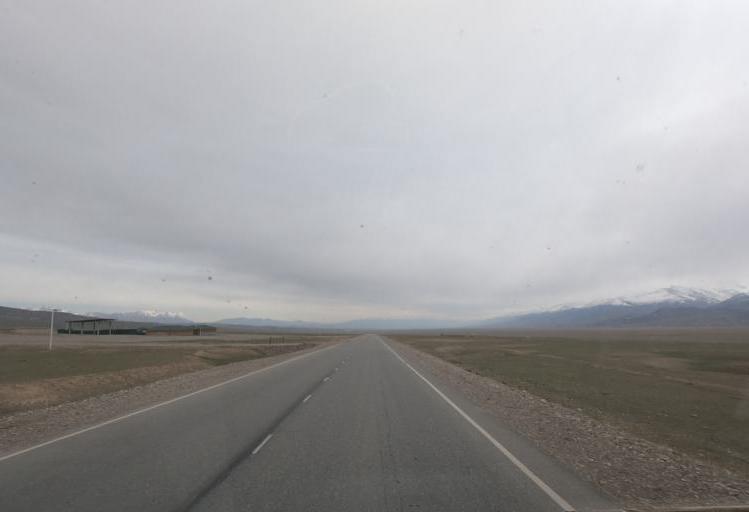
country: KG
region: Naryn
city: At-Bashi
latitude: 41.0067
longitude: 75.3856
